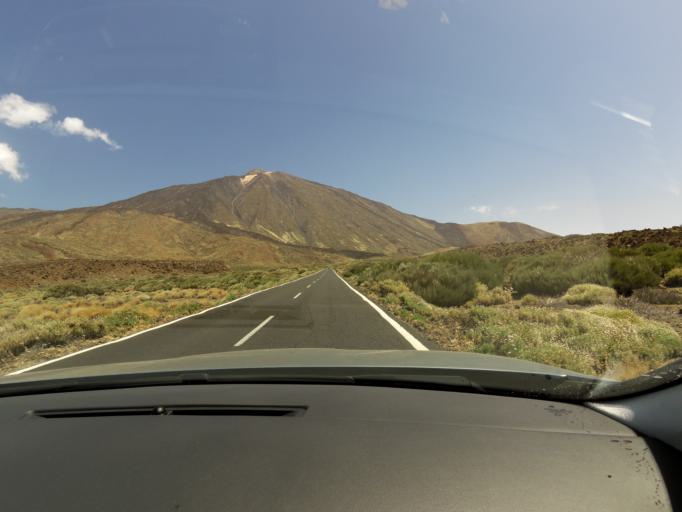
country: ES
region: Canary Islands
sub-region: Provincia de Santa Cruz de Tenerife
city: Vilaflor
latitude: 28.2315
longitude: -16.6291
